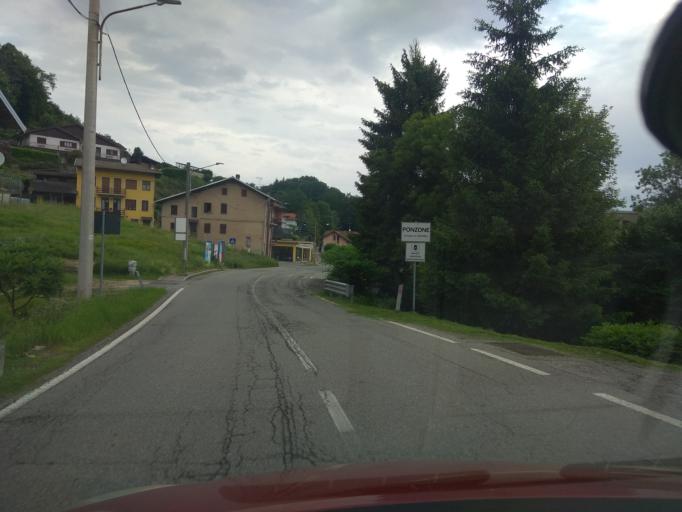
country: IT
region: Piedmont
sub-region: Provincia di Biella
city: Trivero-Prativero-Ponzone
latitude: 45.6459
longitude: 8.1718
